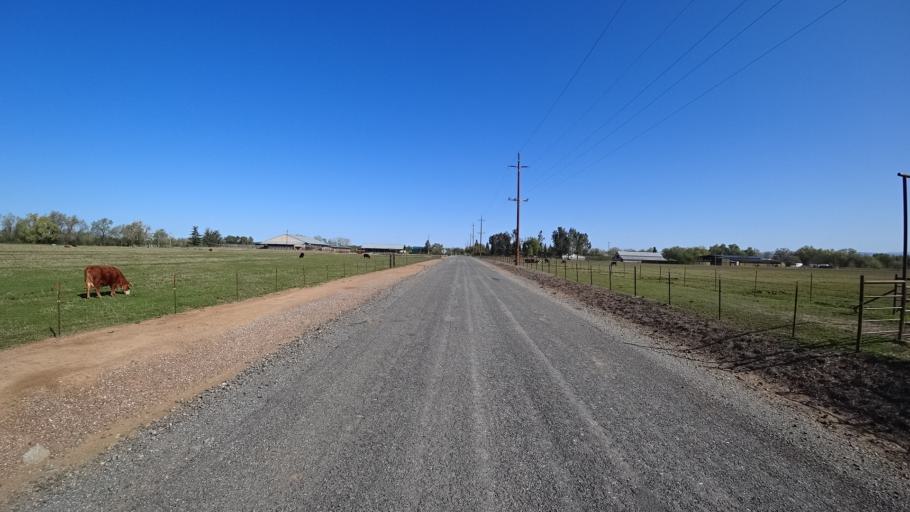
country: US
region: California
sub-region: Glenn County
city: Hamilton City
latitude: 39.7834
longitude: -122.0524
